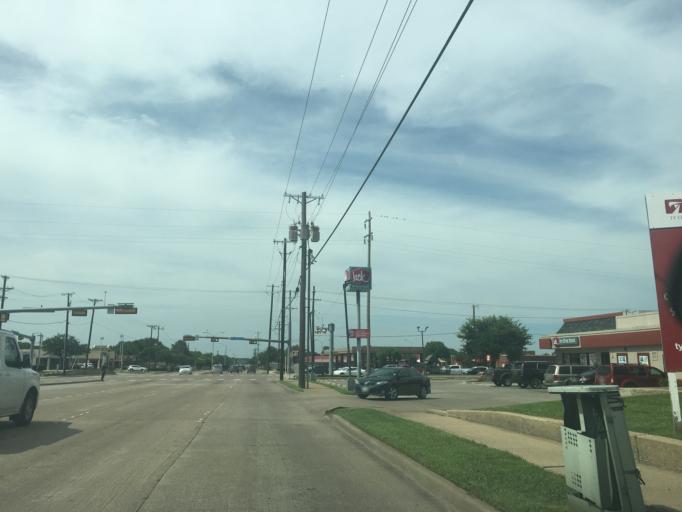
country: US
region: Texas
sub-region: Dallas County
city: Richardson
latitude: 32.9599
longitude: -96.6825
